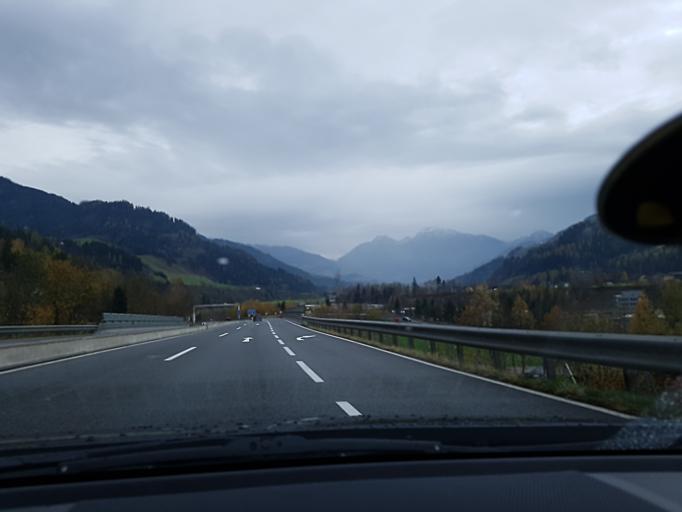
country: AT
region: Salzburg
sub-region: Politischer Bezirk Sankt Johann im Pongau
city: Bischofshofen
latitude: 47.4065
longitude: 13.2249
